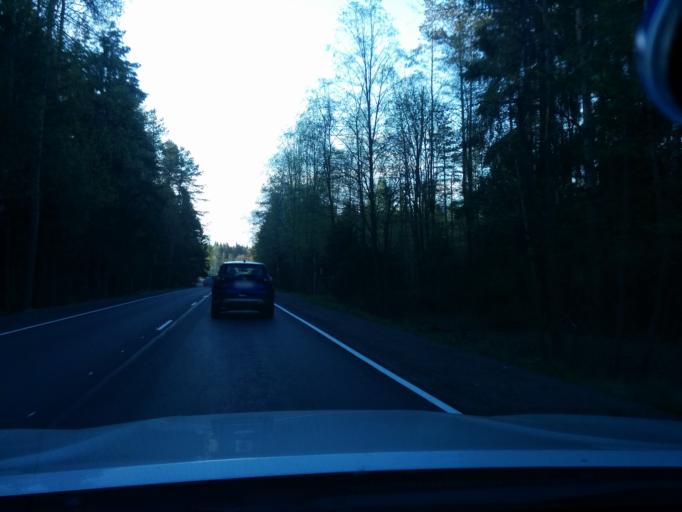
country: RU
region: Leningrad
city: Verkhniye Osel'ki
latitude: 60.2101
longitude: 30.4266
